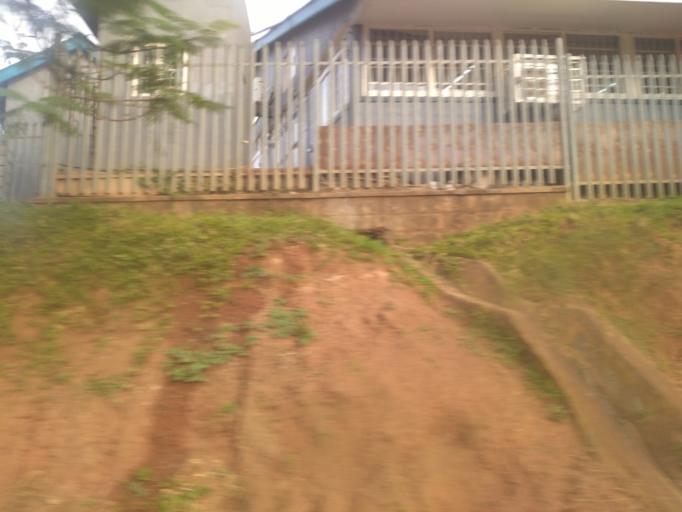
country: UG
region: Central Region
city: Kampala Central Division
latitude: 0.3419
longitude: 32.5766
